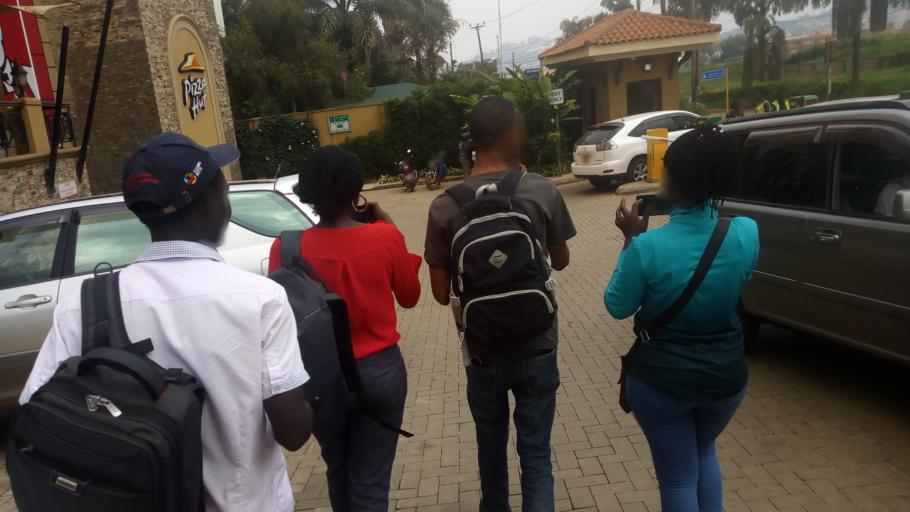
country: UG
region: Central Region
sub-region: Kampala District
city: Kampala
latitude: 0.3198
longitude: 32.6171
